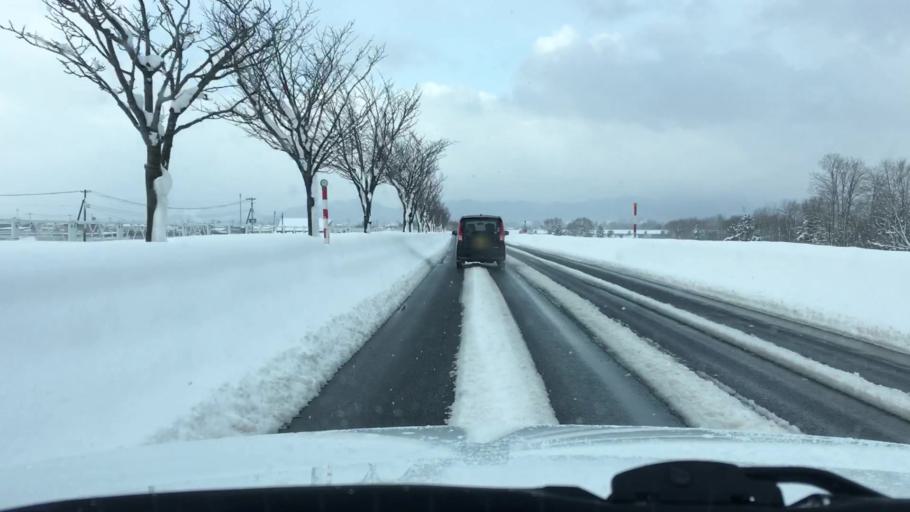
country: JP
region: Aomori
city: Hirosaki
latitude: 40.6338
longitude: 140.4723
